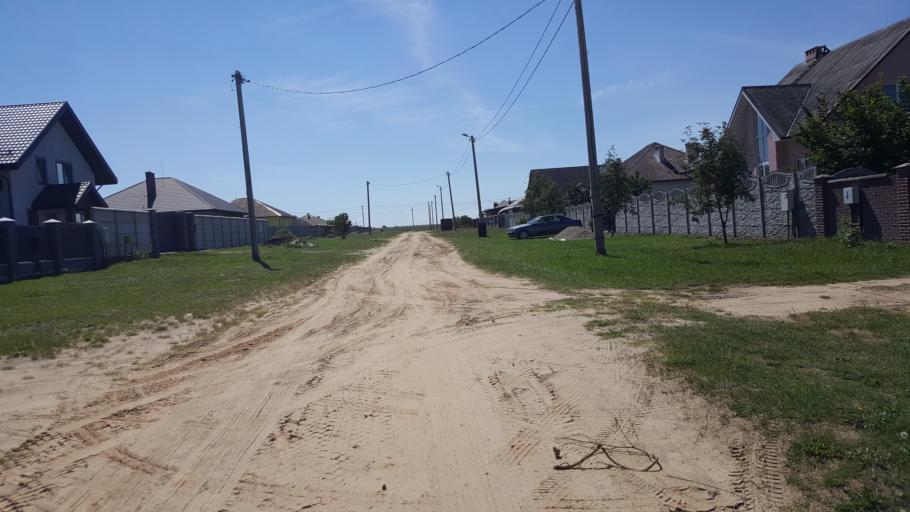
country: BY
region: Brest
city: Charnawchytsy
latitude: 52.2125
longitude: 23.7296
